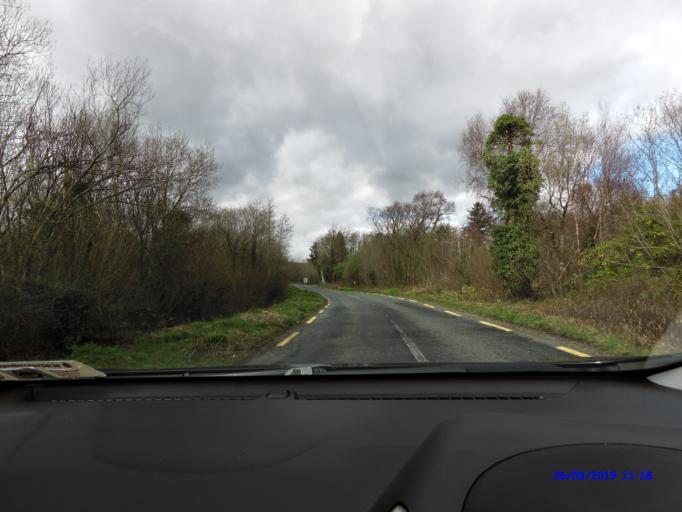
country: IE
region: Connaught
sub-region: Maigh Eo
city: Crossmolina
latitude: 54.0016
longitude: -9.4205
